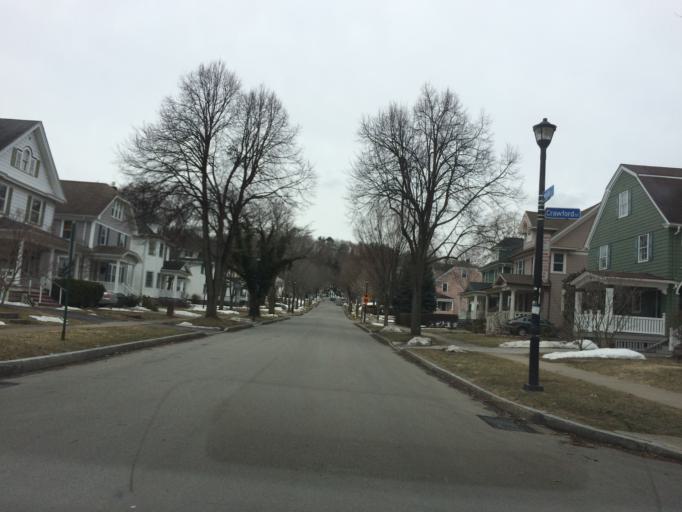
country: US
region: New York
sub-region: Monroe County
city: Rochester
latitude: 43.1367
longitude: -77.6012
